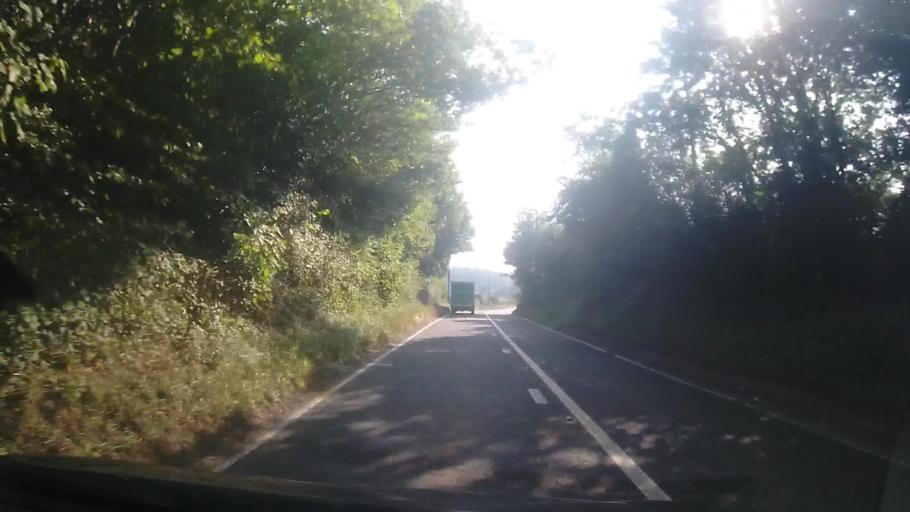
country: GB
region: England
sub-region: Shropshire
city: Much Wenlock
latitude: 52.5988
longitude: -2.5741
